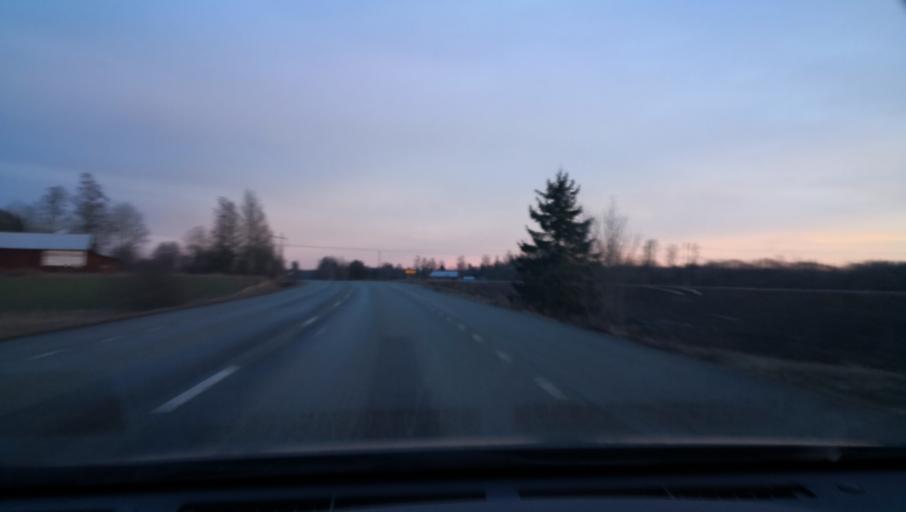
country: SE
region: OErebro
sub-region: Orebro Kommun
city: Vintrosa
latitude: 59.2423
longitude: 15.0667
